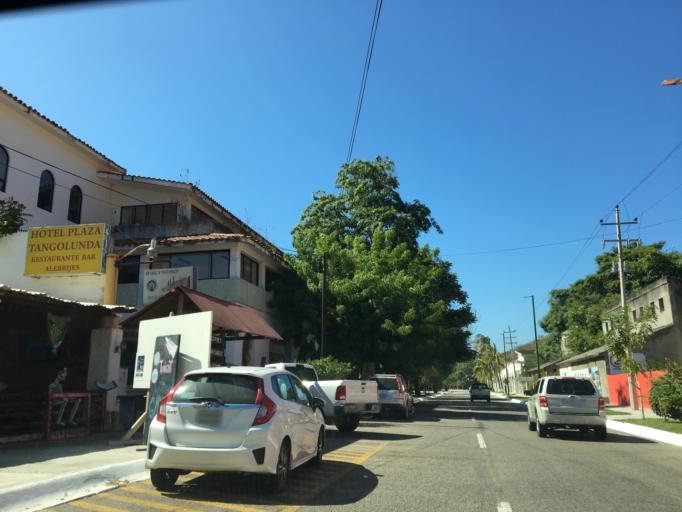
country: MX
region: Oaxaca
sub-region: Santa Maria Huatulco
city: Crucecita
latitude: 15.7754
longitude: -96.0963
